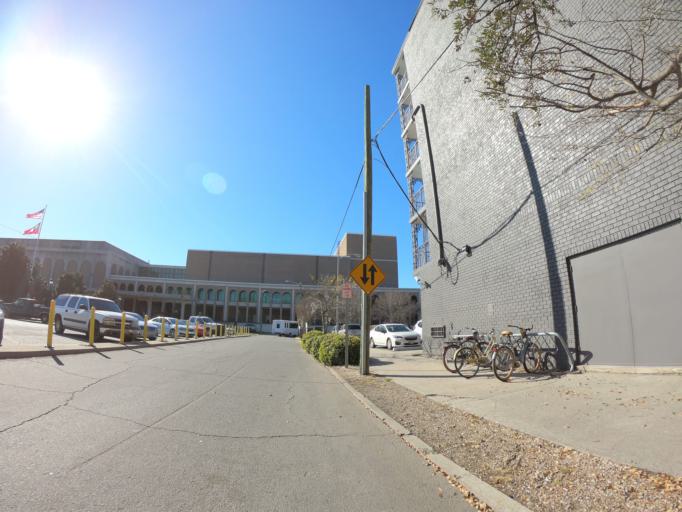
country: US
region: Georgia
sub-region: Chatham County
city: Savannah
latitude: 32.0768
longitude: -81.0958
